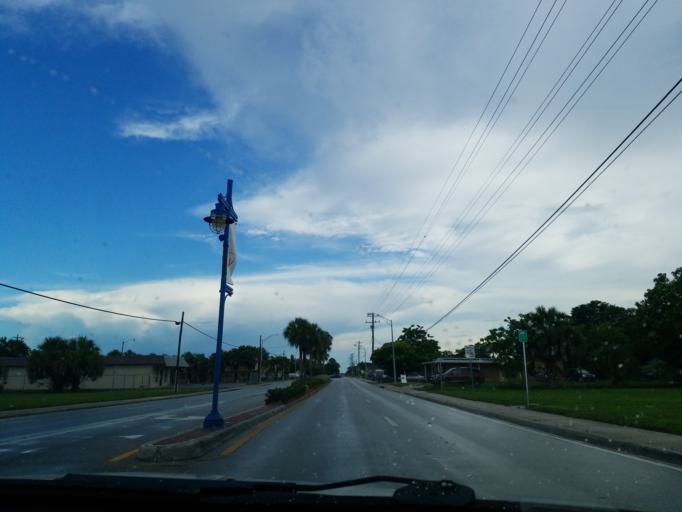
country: US
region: Florida
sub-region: Collier County
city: Immokalee
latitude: 26.4167
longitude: -81.4174
